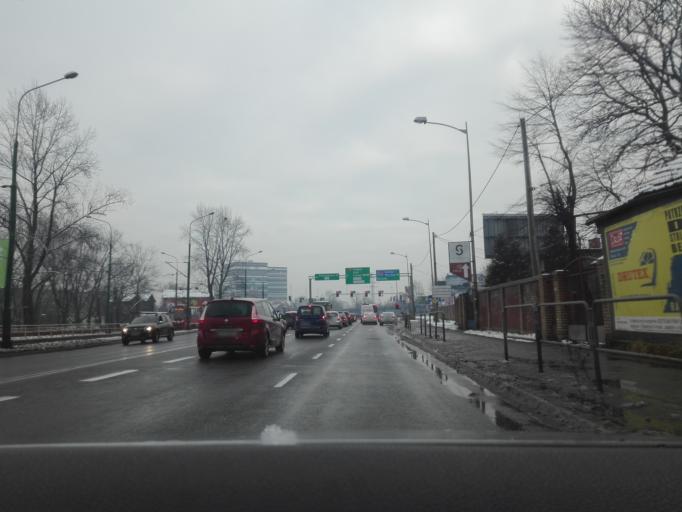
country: PL
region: Silesian Voivodeship
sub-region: Chorzow
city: Chorzow
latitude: 50.2729
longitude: 18.9904
